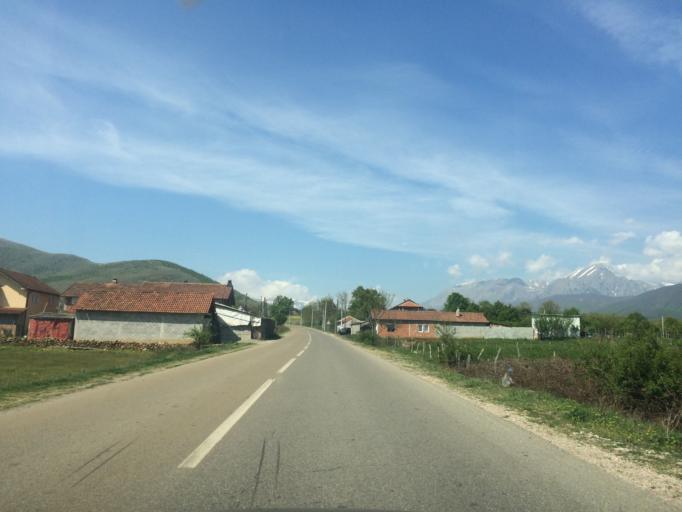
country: XK
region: Gjakova
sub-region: Komuna e Junikut
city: Junik
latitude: 42.4034
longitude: 20.2788
